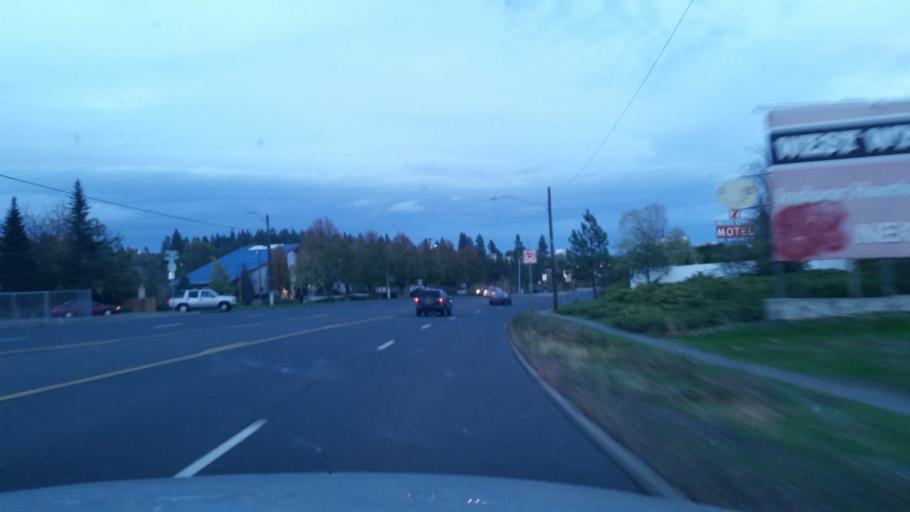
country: US
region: Washington
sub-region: Spokane County
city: Spokane
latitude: 47.6488
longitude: -117.4533
